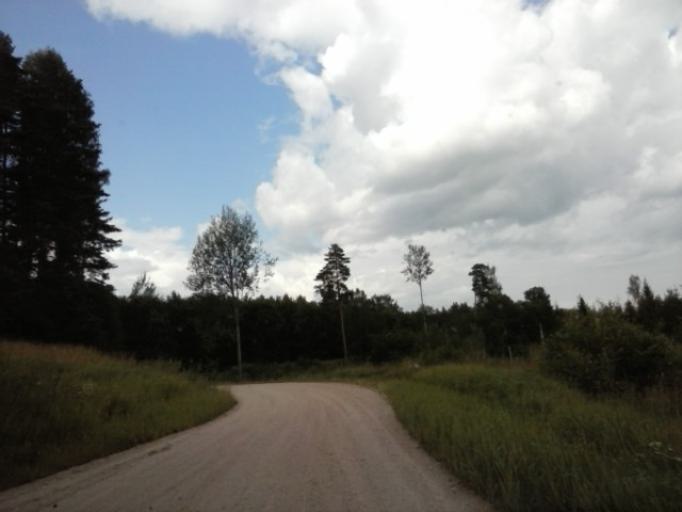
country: EE
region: Vorumaa
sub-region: Voru linn
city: Voru
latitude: 57.7628
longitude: 27.1405
